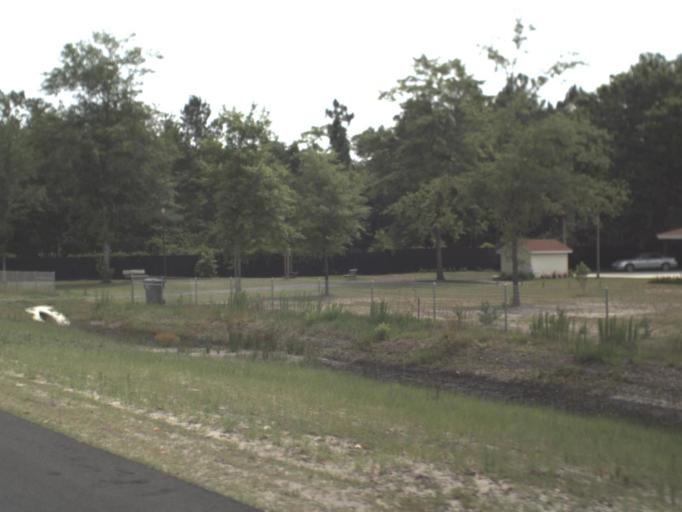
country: US
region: Florida
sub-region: Nassau County
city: Nassau Village-Ratliff
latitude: 30.4514
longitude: -81.9153
